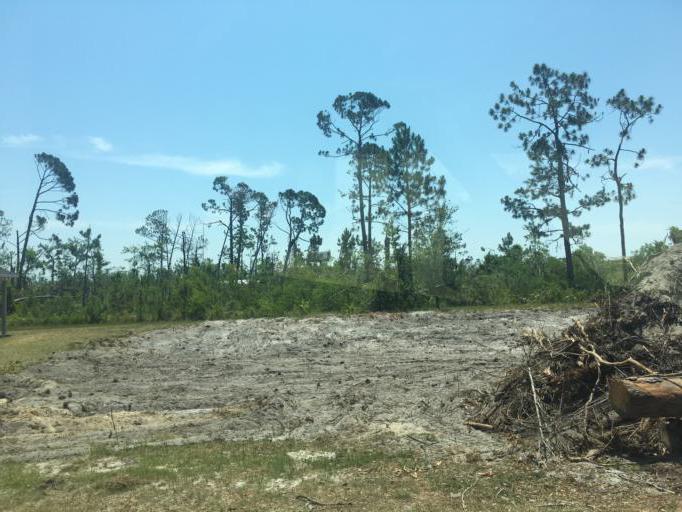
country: US
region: Florida
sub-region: Bay County
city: Hiland Park
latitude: 30.2137
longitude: -85.6511
